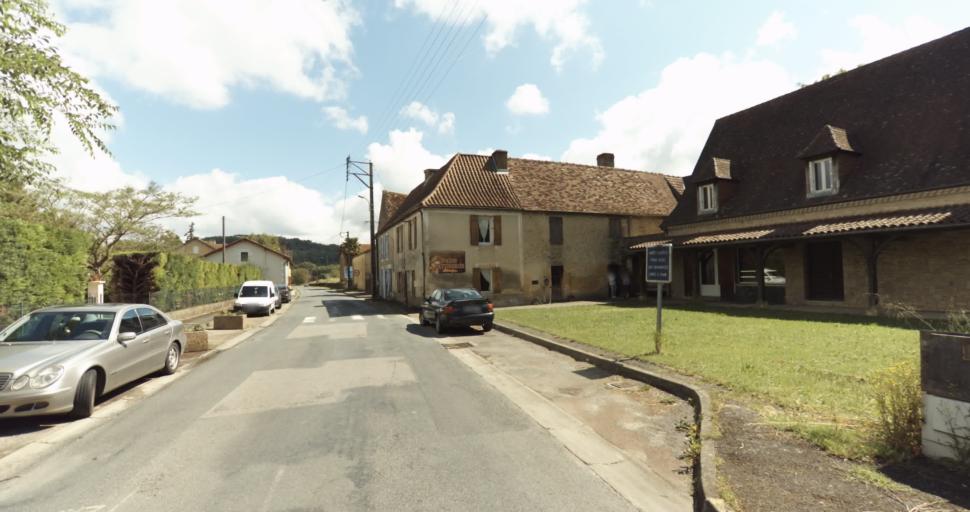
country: FR
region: Aquitaine
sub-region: Departement de la Dordogne
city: Le Bugue
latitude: 44.8482
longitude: 0.9087
